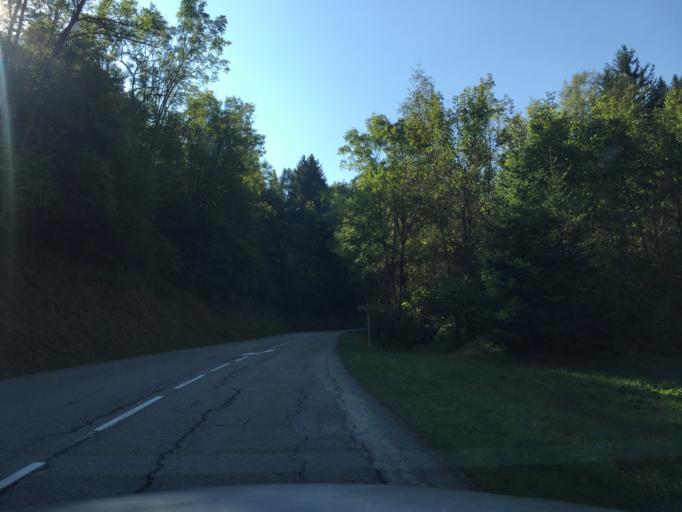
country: FR
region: Rhone-Alpes
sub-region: Departement de la Savoie
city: Bourg-Saint-Maurice
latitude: 45.5669
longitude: 6.7444
